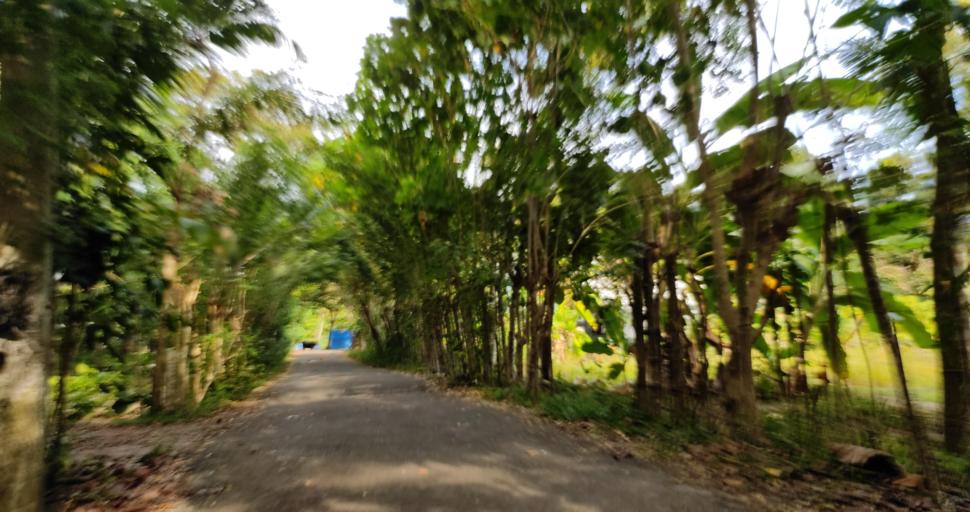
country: IN
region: Kerala
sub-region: Alappuzha
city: Shertallai
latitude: 9.6148
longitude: 76.3449
